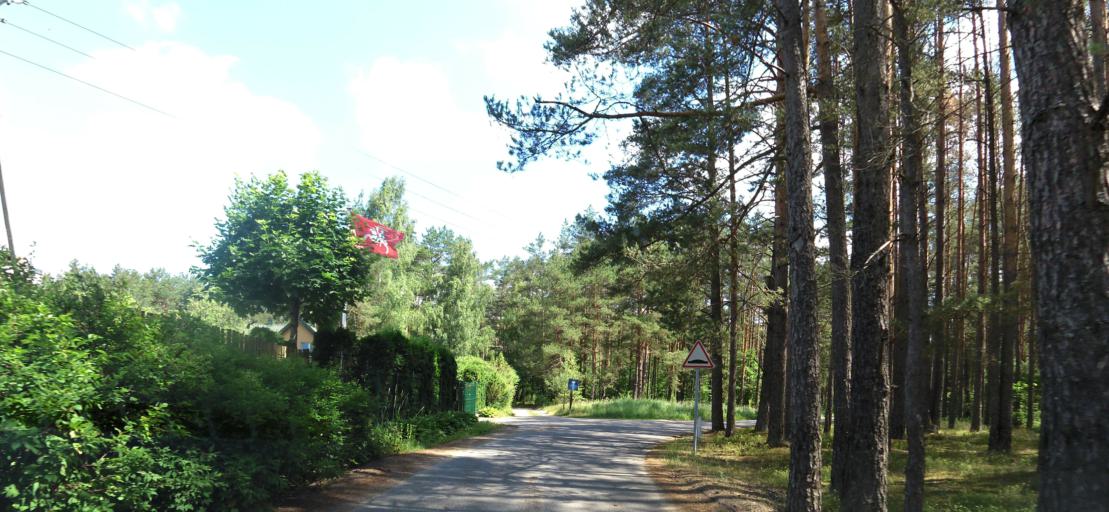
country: LT
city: Nemencine
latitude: 54.8212
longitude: 25.4006
